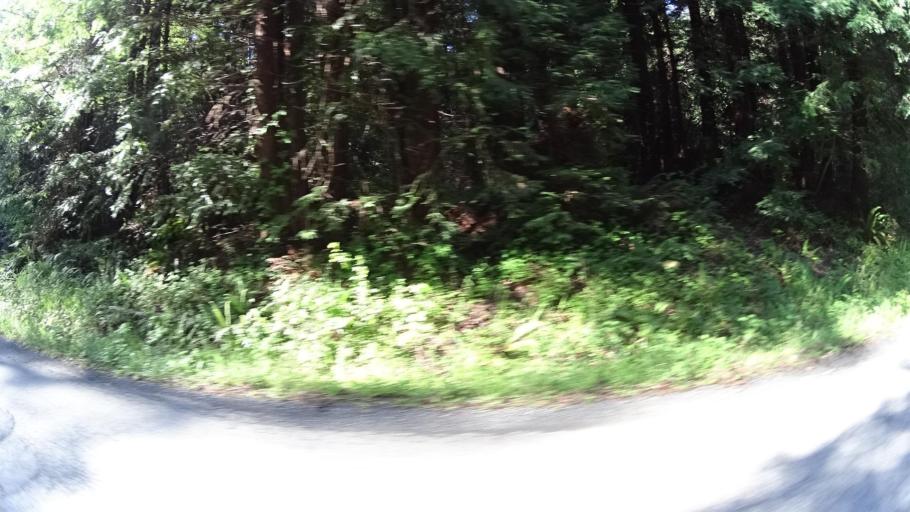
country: US
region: California
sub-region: Humboldt County
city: Rio Dell
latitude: 40.4376
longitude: -123.9688
